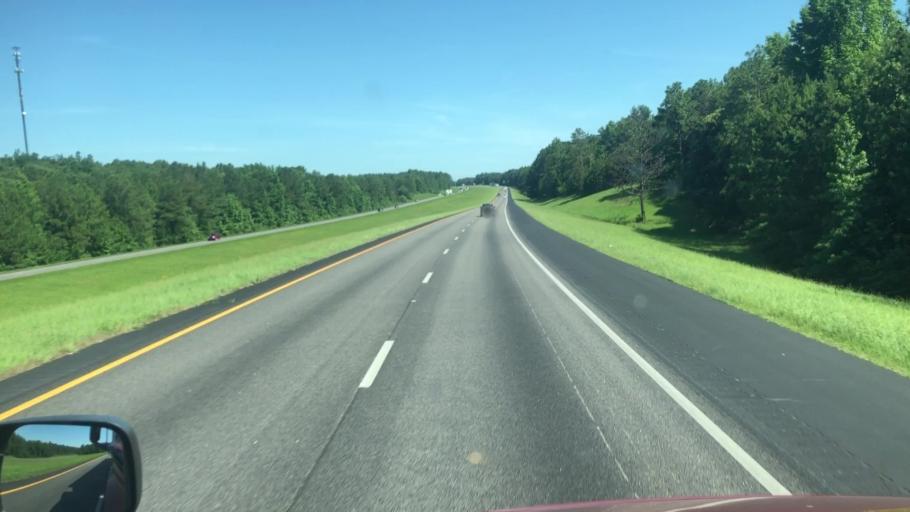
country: US
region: Alabama
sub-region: Autauga County
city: Pine Level
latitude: 32.5266
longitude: -86.4415
